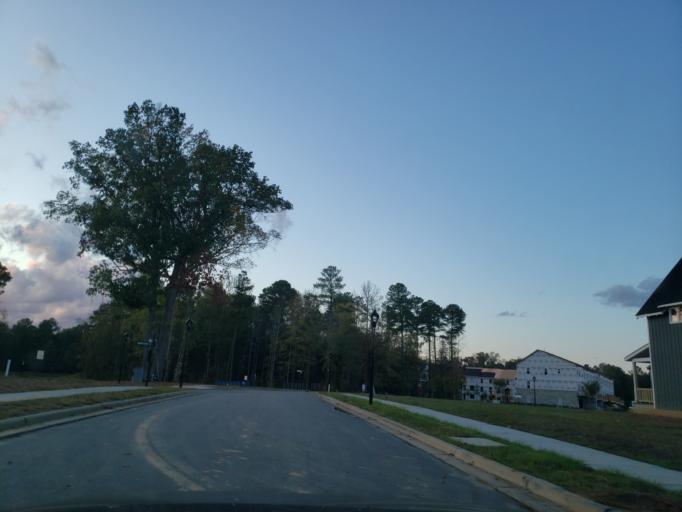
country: US
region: North Carolina
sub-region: Orange County
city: Chapel Hill
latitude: 35.8781
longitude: -78.9561
